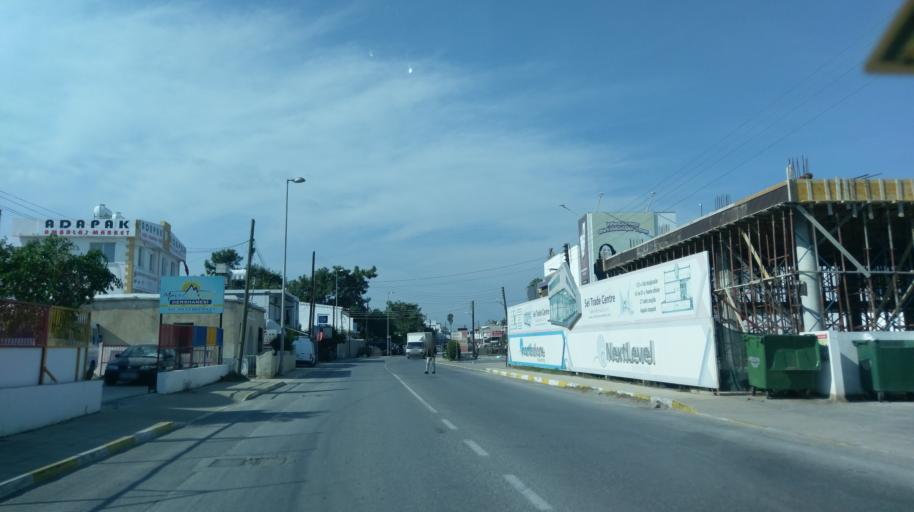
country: CY
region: Keryneia
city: Kyrenia
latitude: 35.3419
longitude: 33.2741
